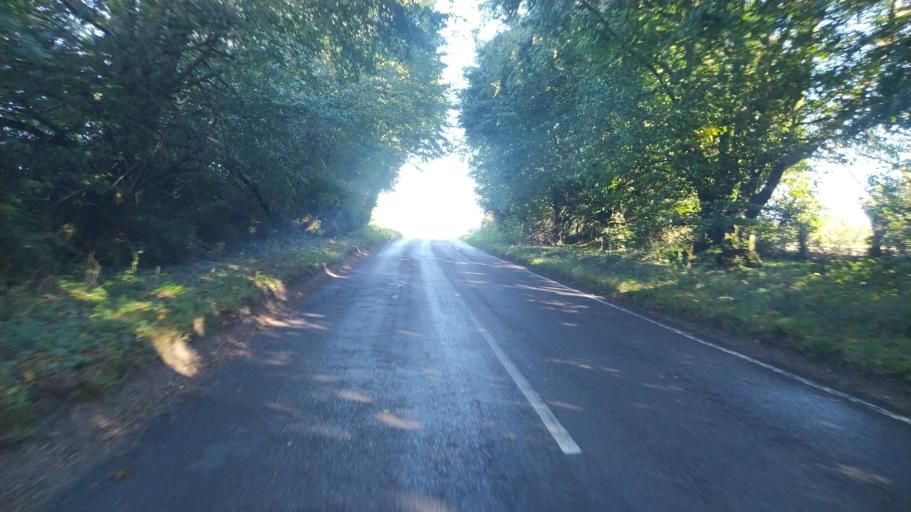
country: GB
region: England
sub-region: Dorset
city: Blandford Forum
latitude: 50.7819
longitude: -2.1984
